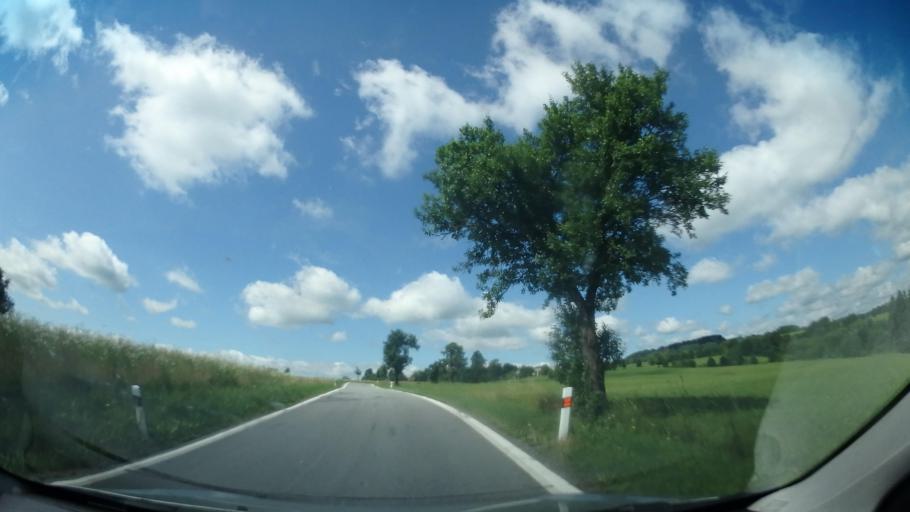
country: CZ
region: Vysocina
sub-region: Okres Zd'ar nad Sazavou
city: Nove Mesto na Morave
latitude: 49.6437
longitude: 16.1031
